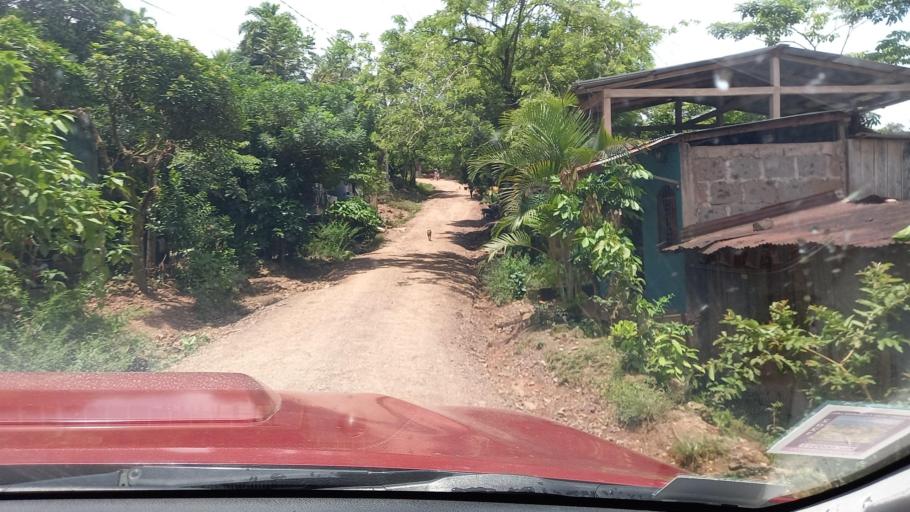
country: NI
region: Atlantico Norte (RAAN)
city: Waslala
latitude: 13.3389
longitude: -85.3720
